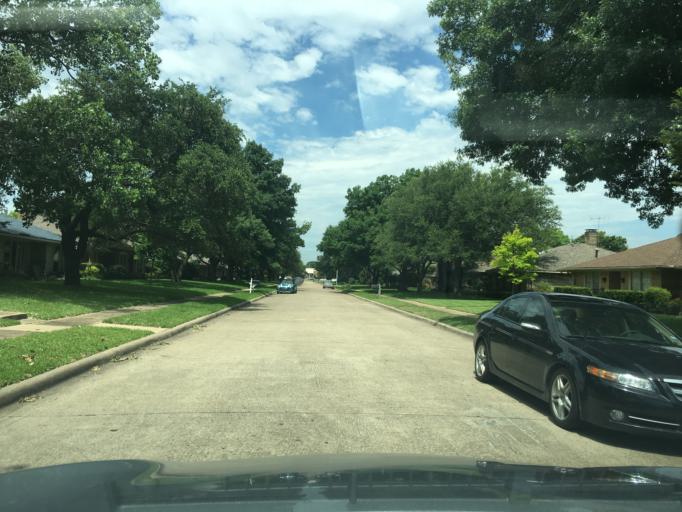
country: US
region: Texas
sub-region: Dallas County
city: Richardson
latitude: 32.9396
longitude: -96.7015
